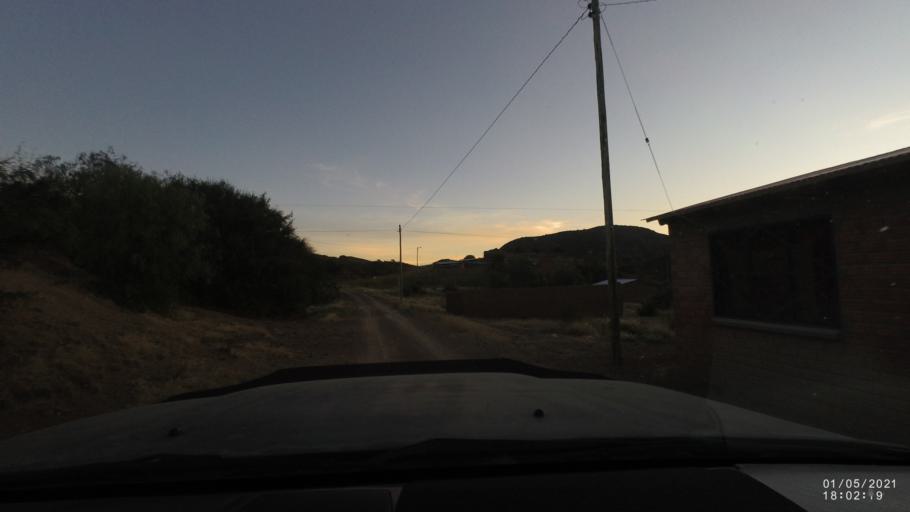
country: BO
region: Cochabamba
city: Capinota
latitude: -17.6873
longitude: -66.1736
